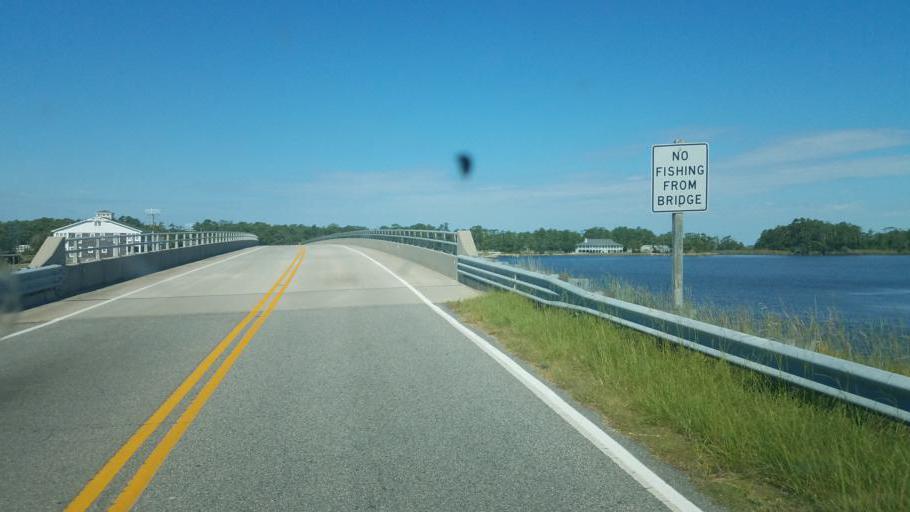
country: US
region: North Carolina
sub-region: Dare County
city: Kill Devil Hills
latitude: 36.0154
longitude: -75.6858
